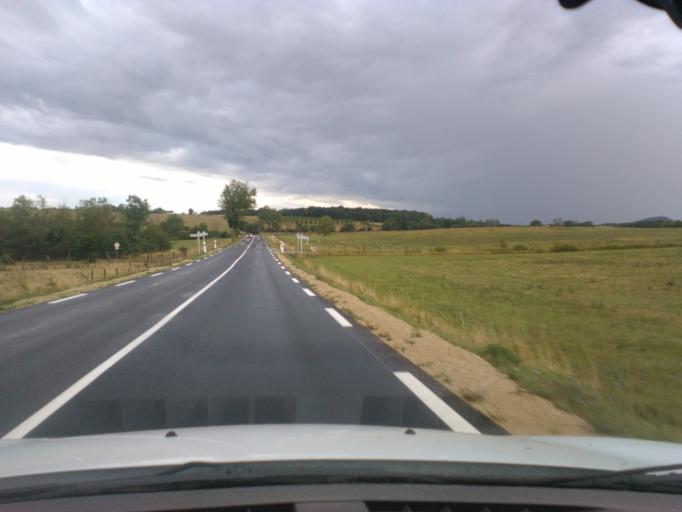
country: FR
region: Lorraine
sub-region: Departement de Meurthe-et-Moselle
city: Vezelise
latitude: 48.4336
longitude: 6.1250
